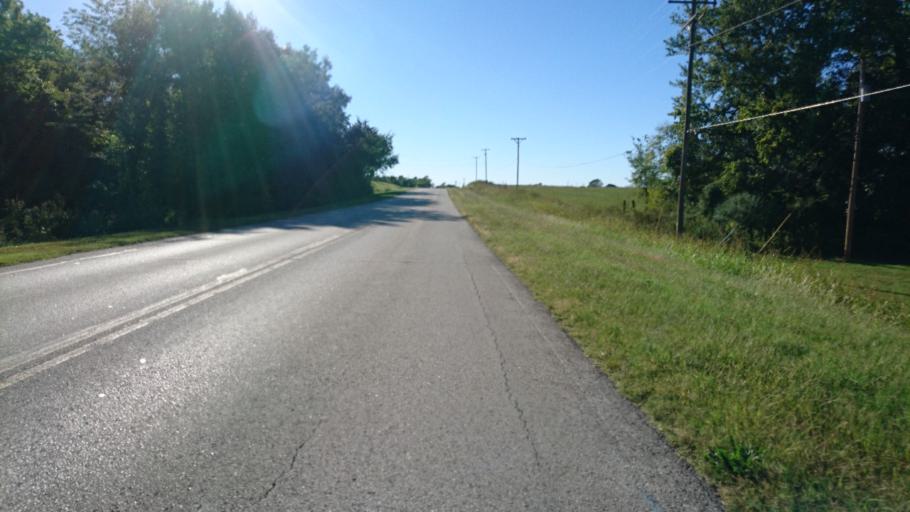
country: US
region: Missouri
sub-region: Jasper County
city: Carthage
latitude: 37.1733
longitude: -94.3588
